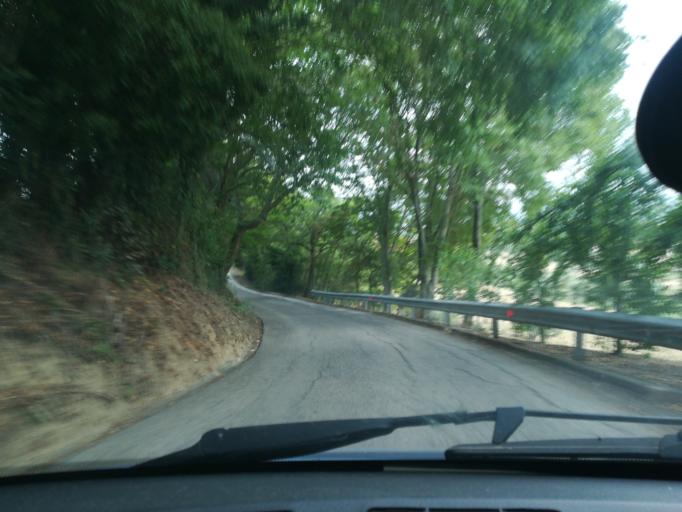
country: IT
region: The Marches
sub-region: Provincia di Macerata
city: Piediripa
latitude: 43.2946
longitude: 13.4850
